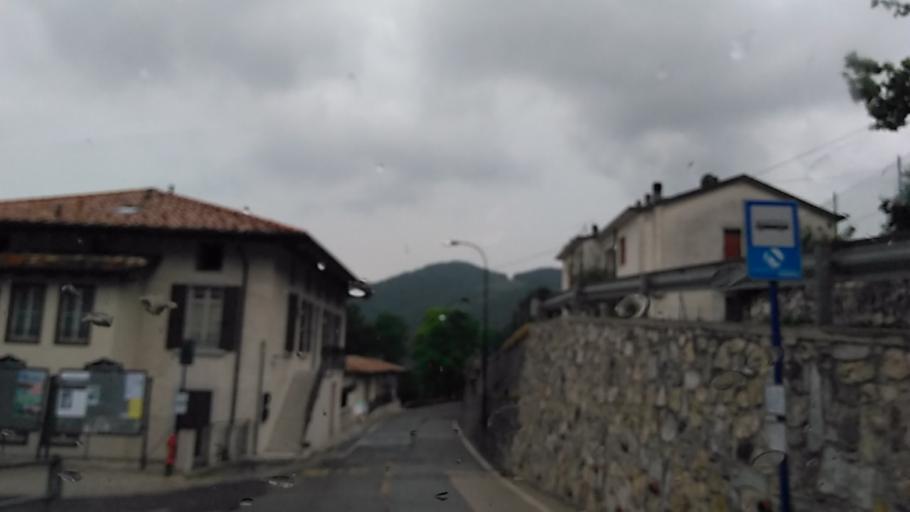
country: IT
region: Lombardy
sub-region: Provincia di Brescia
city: Pieve
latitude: 45.7913
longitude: 10.7410
